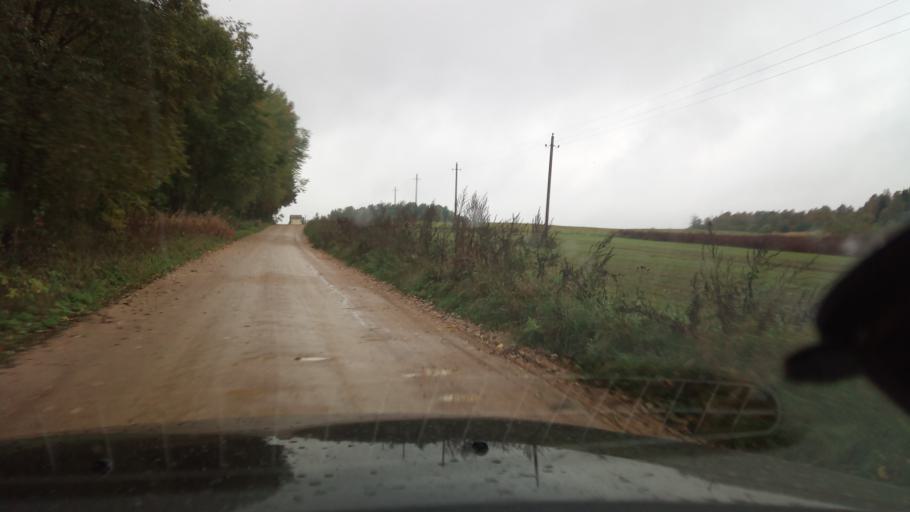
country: LT
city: Skaidiskes
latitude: 54.5544
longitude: 25.4839
